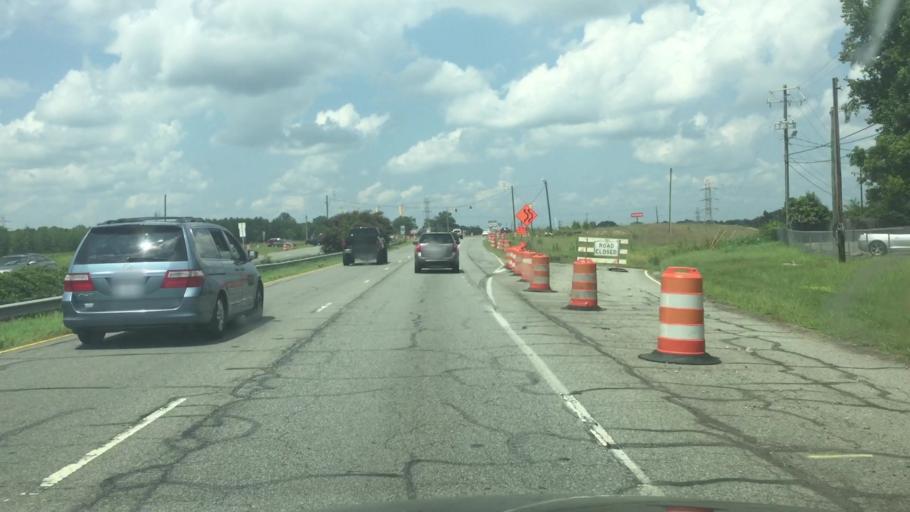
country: US
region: North Carolina
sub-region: Cabarrus County
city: Concord
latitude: 35.4431
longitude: -80.6086
